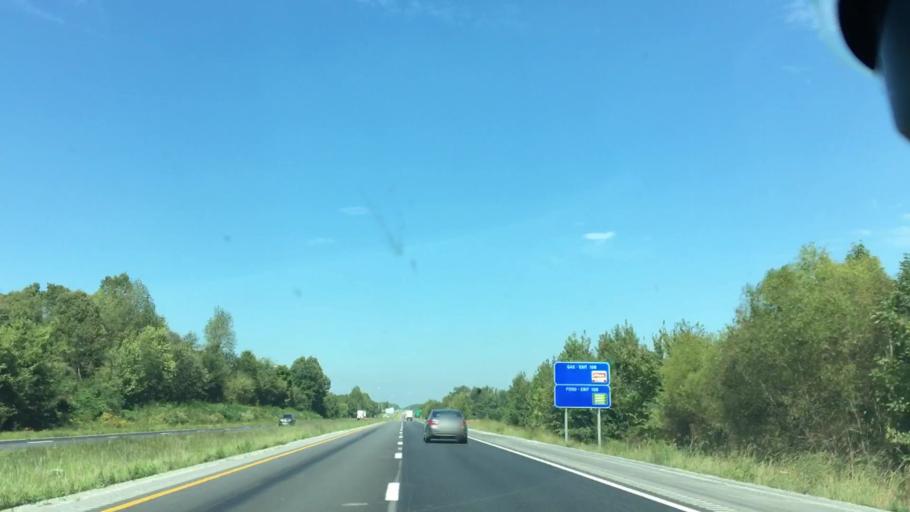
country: US
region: Kentucky
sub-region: Hopkins County
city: Nortonville
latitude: 37.2358
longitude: -87.4464
